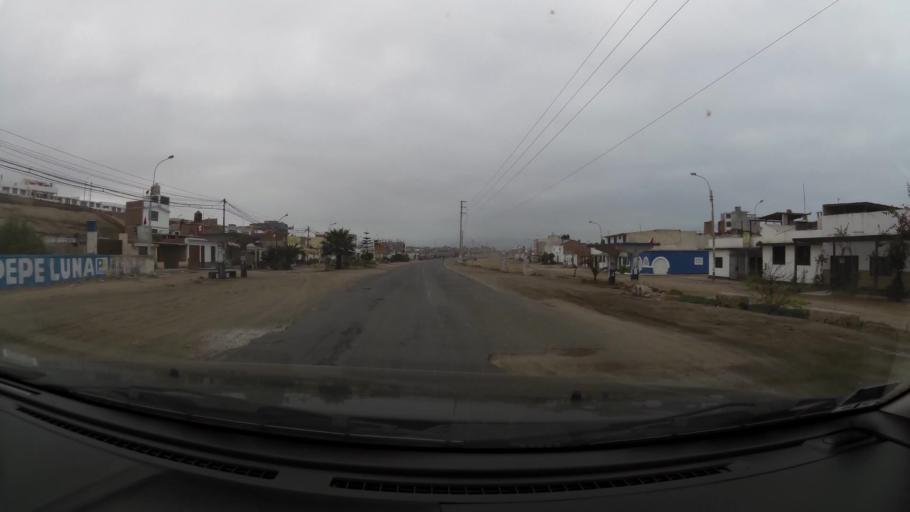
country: PE
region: Lima
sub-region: Lima
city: San Bartolo
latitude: -12.3586
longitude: -76.8002
